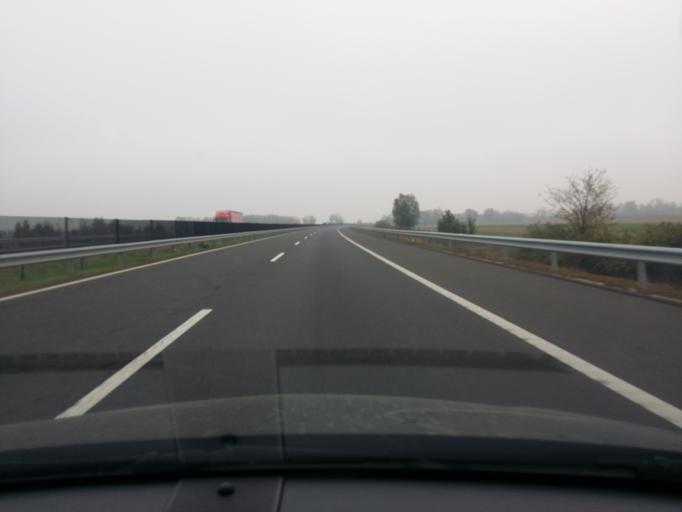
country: HU
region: Szabolcs-Szatmar-Bereg
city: Nagycserkesz
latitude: 47.9035
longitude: 21.5103
